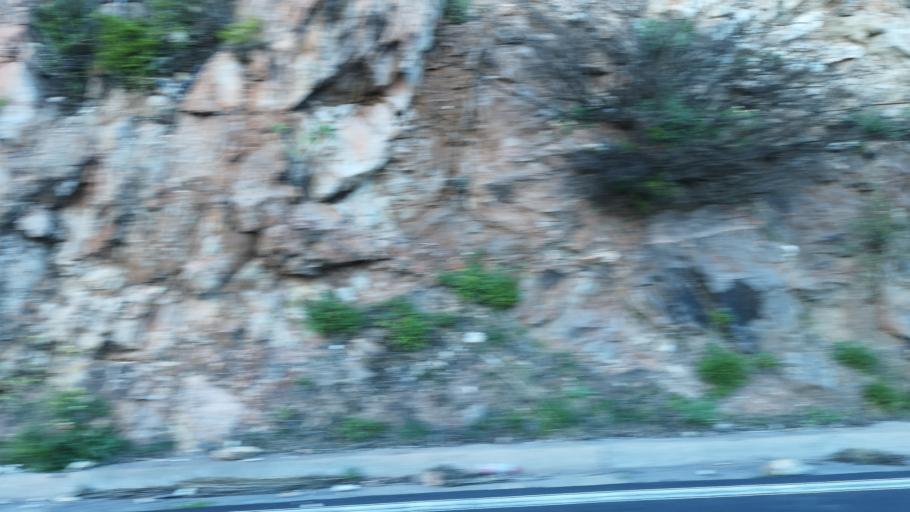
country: ES
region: Canary Islands
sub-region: Provincia de Santa Cruz de Tenerife
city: Alajero
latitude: 28.0878
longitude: -17.2509
